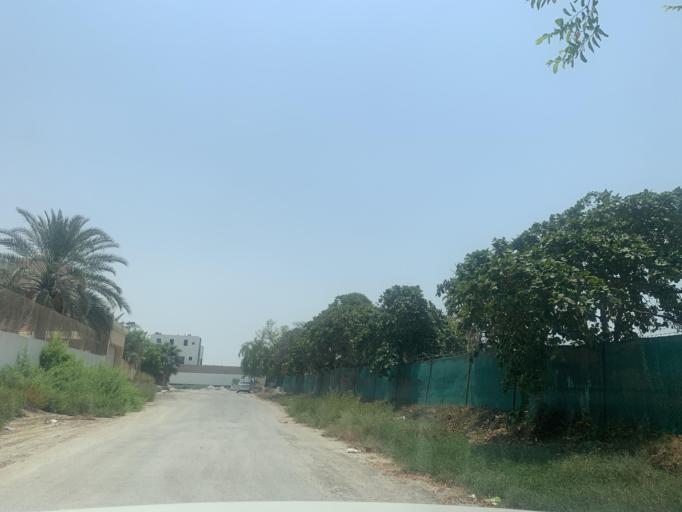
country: BH
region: Central Governorate
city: Madinat Hamad
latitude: 26.1483
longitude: 50.4627
